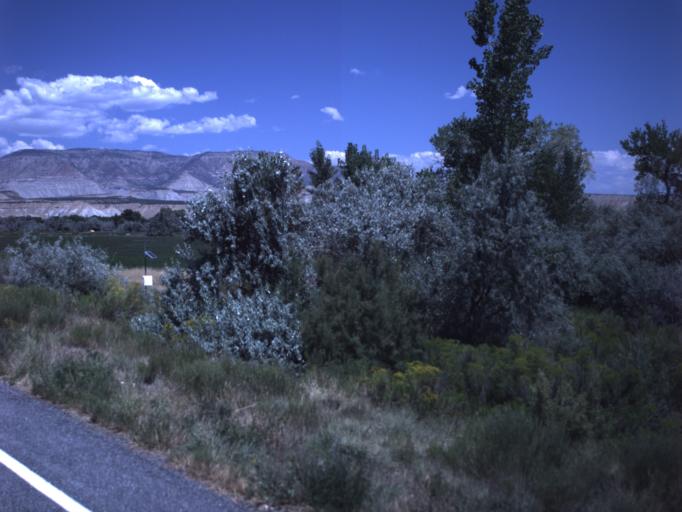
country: US
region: Utah
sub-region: Emery County
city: Orangeville
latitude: 39.2180
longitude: -111.0670
